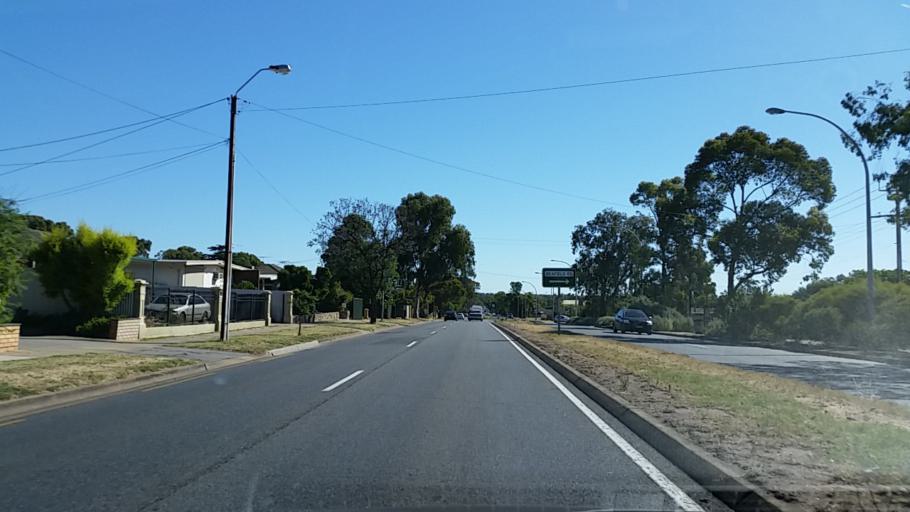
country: AU
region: South Australia
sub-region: Salisbury
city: Ingle Farm
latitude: -34.8015
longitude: 138.6540
